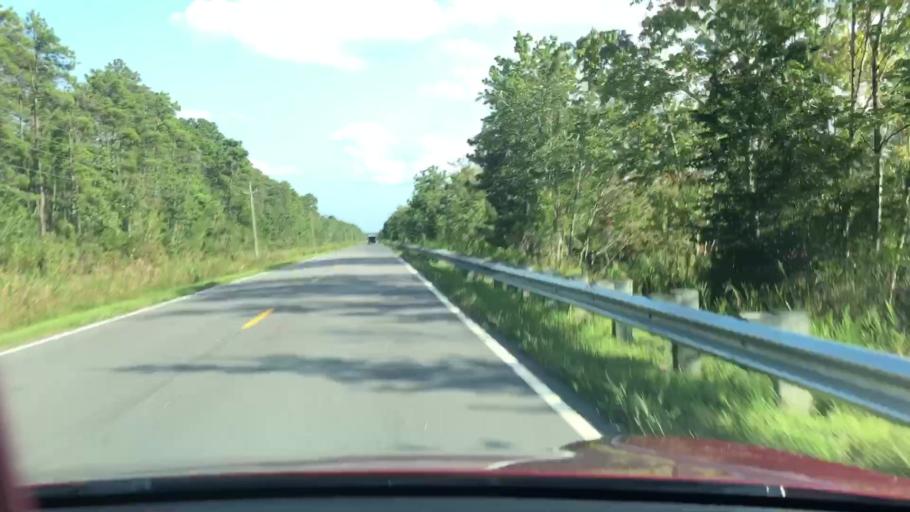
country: US
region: North Carolina
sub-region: Dare County
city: Wanchese
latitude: 35.8025
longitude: -75.7835
